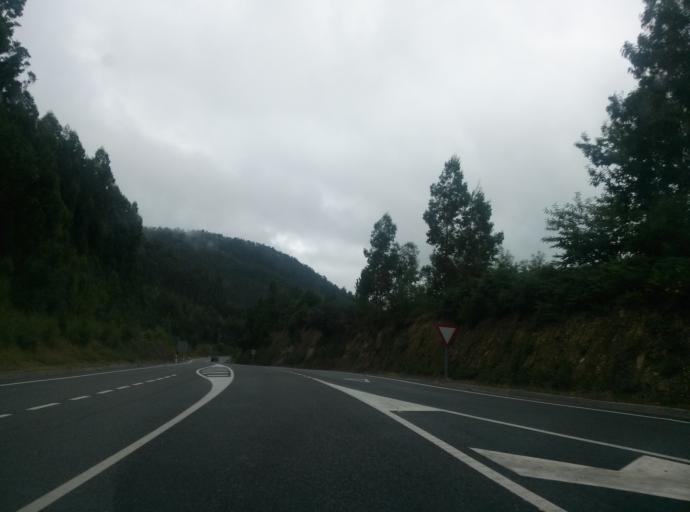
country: ES
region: Galicia
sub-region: Provincia de Lugo
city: Viveiro
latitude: 43.5748
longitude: -7.6336
